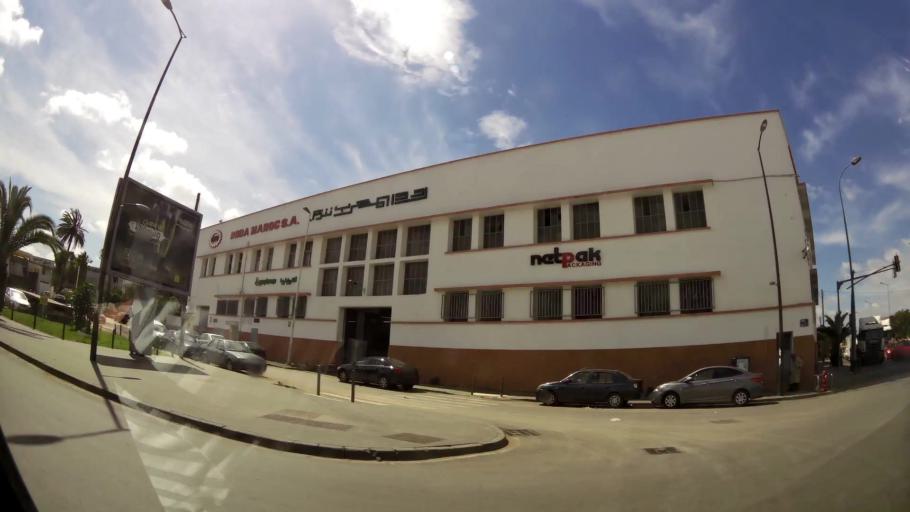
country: MA
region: Grand Casablanca
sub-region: Casablanca
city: Casablanca
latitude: 33.6039
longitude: -7.5422
